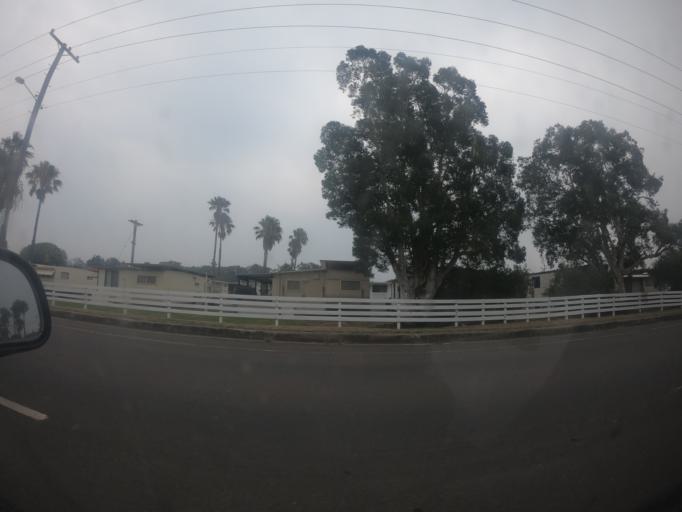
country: AU
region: New South Wales
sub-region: Shellharbour
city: Barrack Heights
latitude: -34.5666
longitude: 150.8667
